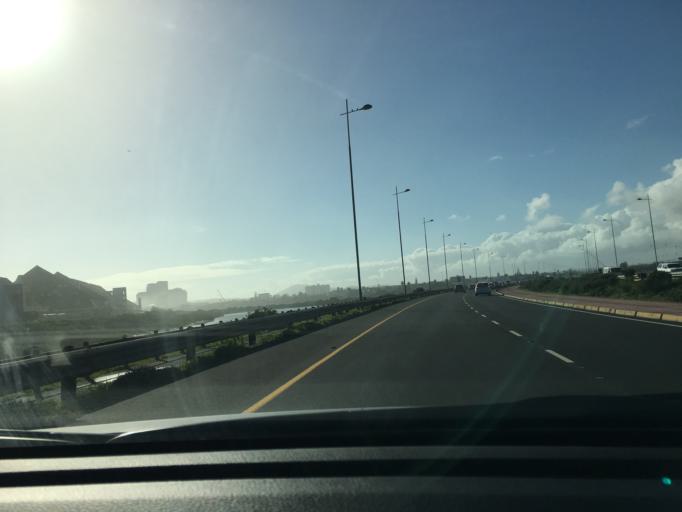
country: ZA
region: Western Cape
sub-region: City of Cape Town
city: Sunset Beach
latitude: -33.8336
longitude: 18.4840
